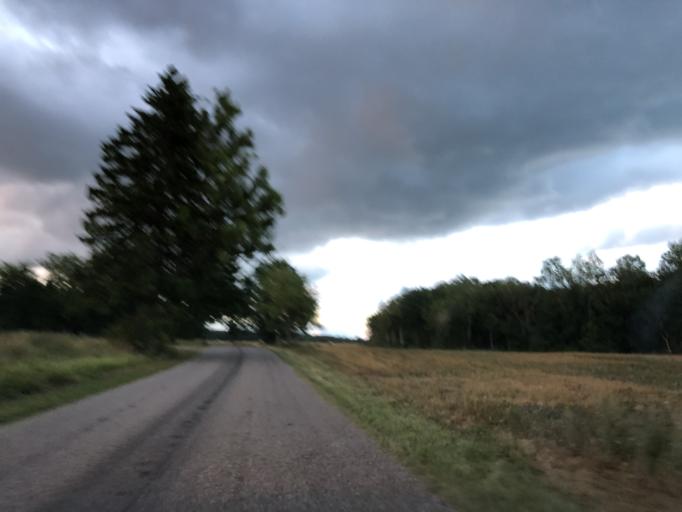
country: EE
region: Laeaene
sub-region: Ridala Parish
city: Uuemoisa
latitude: 58.8943
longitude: 23.6776
